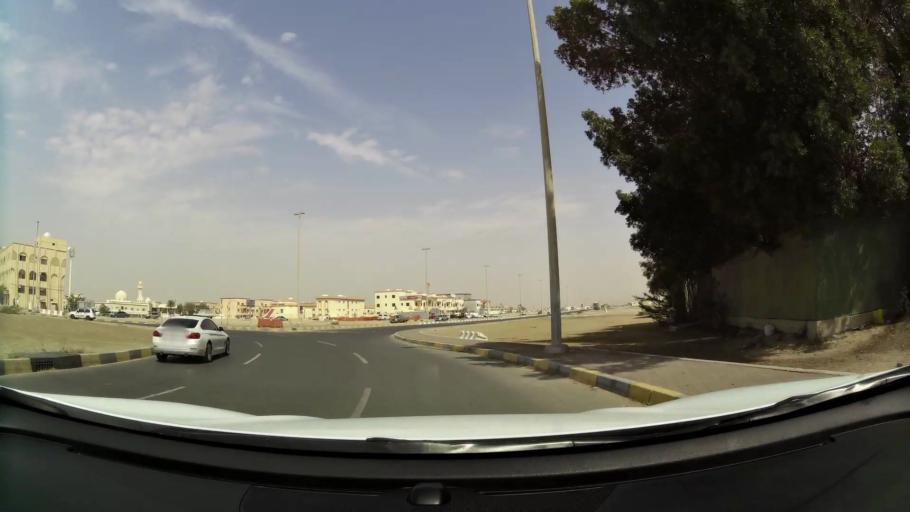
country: AE
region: Abu Dhabi
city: Abu Dhabi
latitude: 24.2959
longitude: 54.6299
